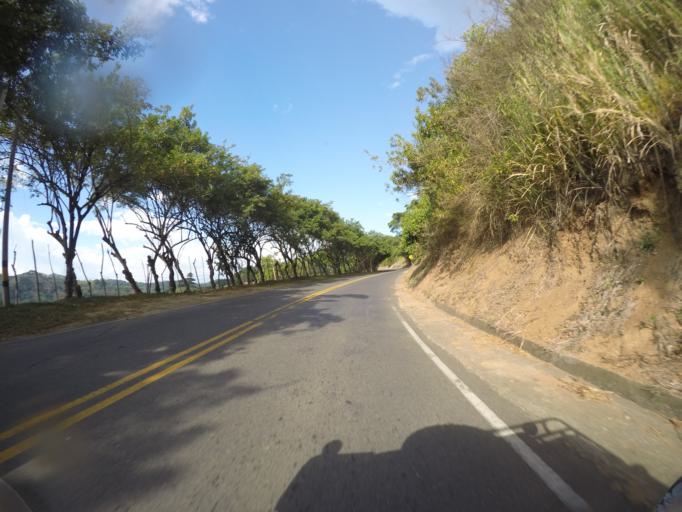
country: CO
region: Valle del Cauca
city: Cartago
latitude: 4.7274
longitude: -75.8759
